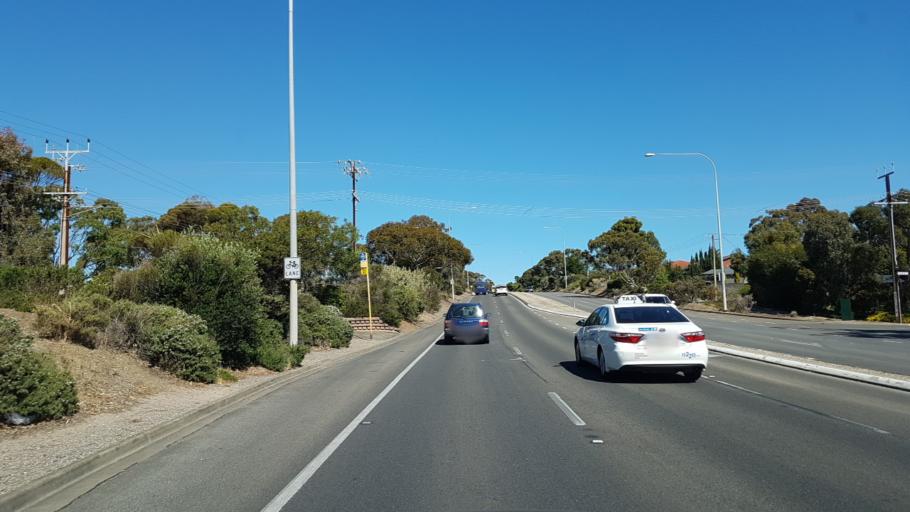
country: AU
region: South Australia
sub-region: Onkaparinga
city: Bedford Park
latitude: -35.0381
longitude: 138.5669
